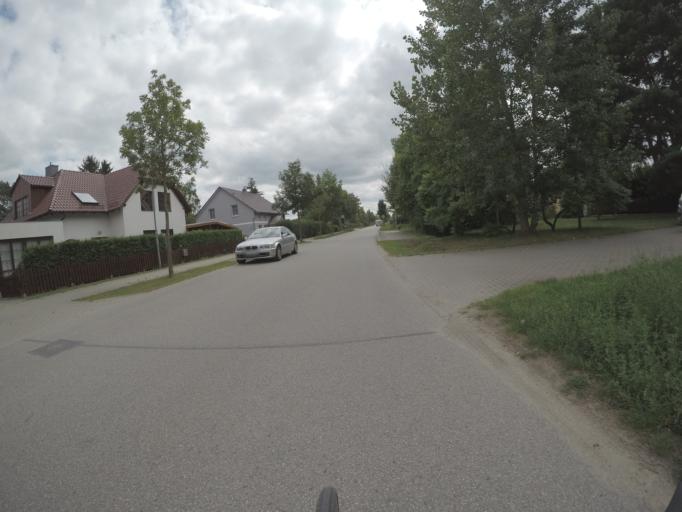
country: DE
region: Brandenburg
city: Brieselang
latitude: 52.6040
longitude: 12.9876
